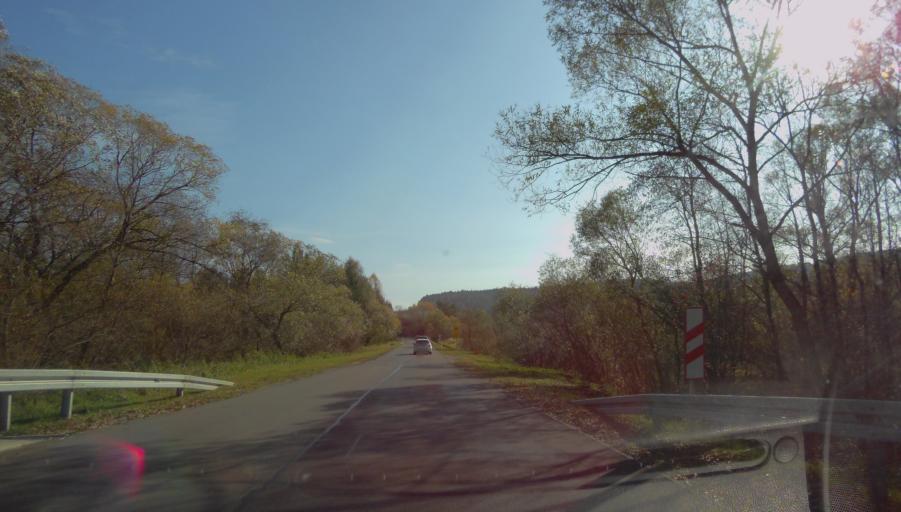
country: PL
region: Subcarpathian Voivodeship
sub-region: Powiat sanocki
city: Komancza
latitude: 49.2438
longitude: 22.1086
